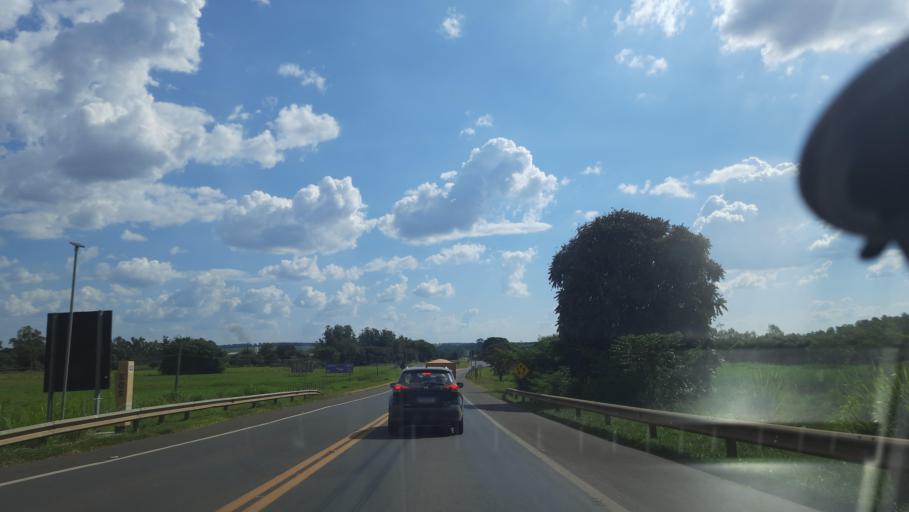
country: BR
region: Sao Paulo
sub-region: Casa Branca
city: Casa Branca
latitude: -21.7402
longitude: -46.9773
